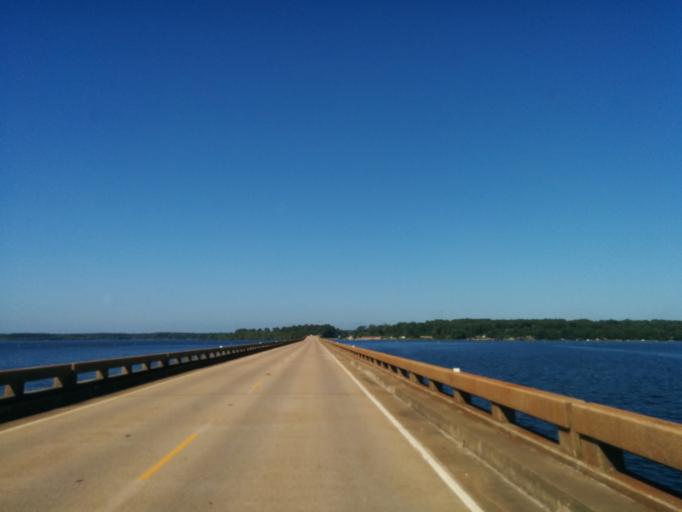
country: US
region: Texas
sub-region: Sabine County
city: Milam
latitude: 31.4701
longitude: -93.7390
